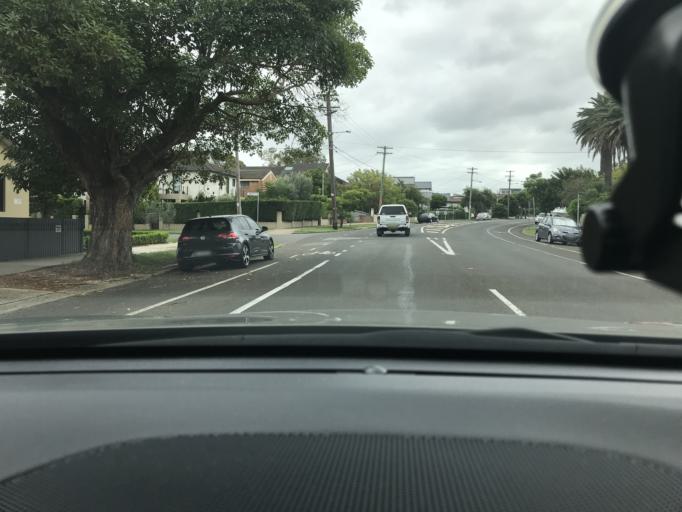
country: AU
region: New South Wales
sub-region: Canada Bay
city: Wareemba
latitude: -33.8503
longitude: 151.1284
